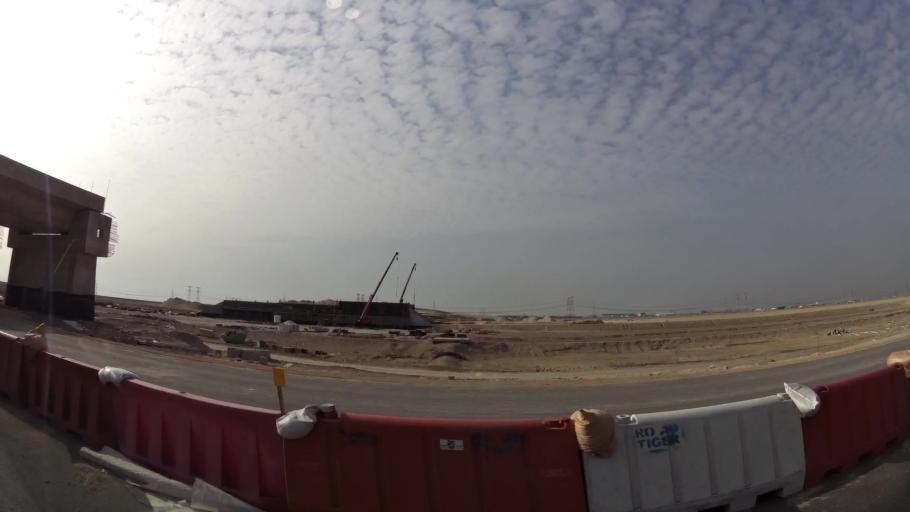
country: AE
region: Abu Dhabi
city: Abu Dhabi
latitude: 24.2472
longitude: 54.4735
